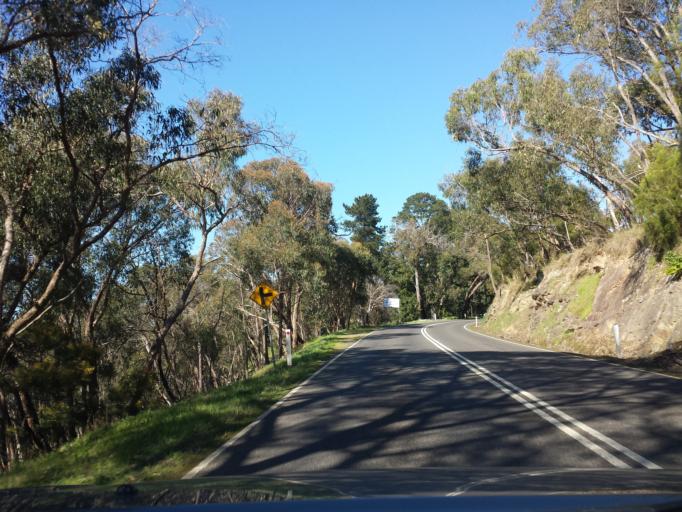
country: AU
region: Victoria
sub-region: Yarra Ranges
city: Yarra Glen
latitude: -37.6505
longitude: 145.3482
